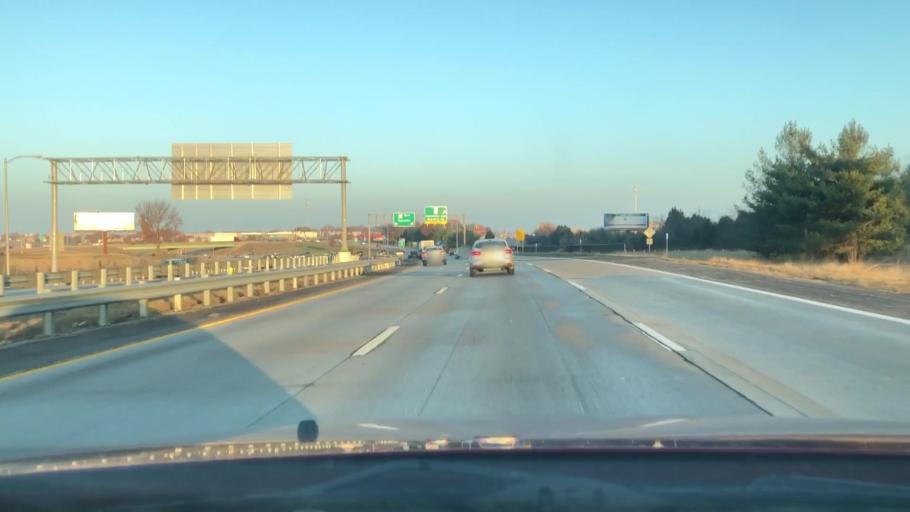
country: US
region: Missouri
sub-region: Greene County
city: Springfield
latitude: 37.1367
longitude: -93.2481
